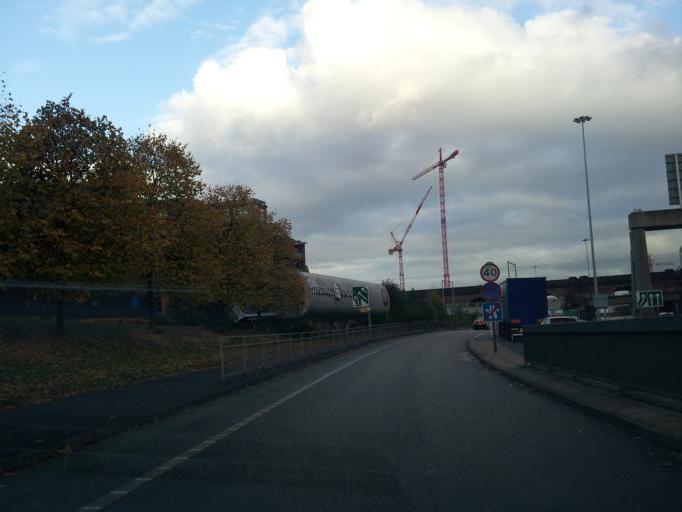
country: GB
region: England
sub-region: Manchester
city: Hulme
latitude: 53.4728
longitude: -2.2594
